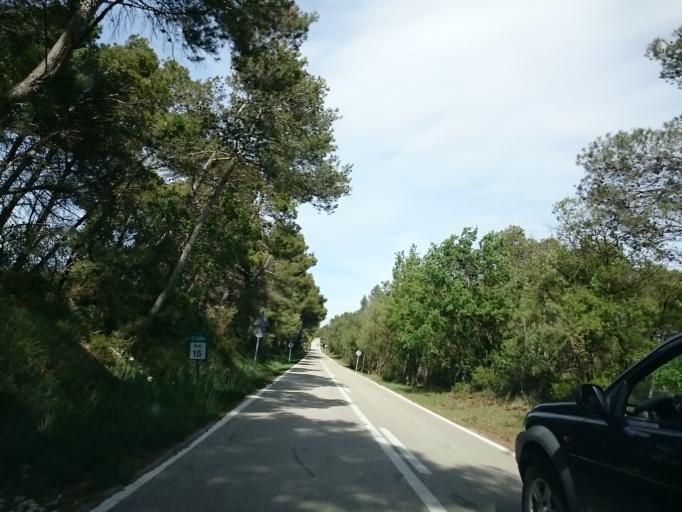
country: ES
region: Catalonia
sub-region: Provincia de Barcelona
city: Bellprat
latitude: 41.5651
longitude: 1.4450
